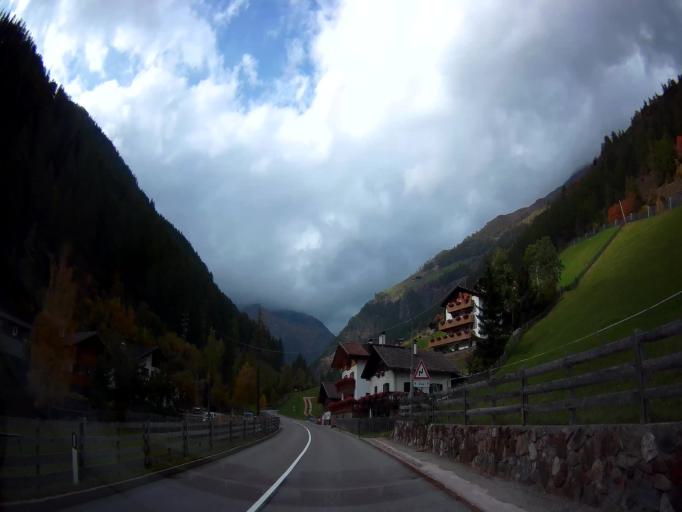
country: IT
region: Trentino-Alto Adige
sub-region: Bolzano
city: Senales
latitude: 46.7113
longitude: 10.8984
